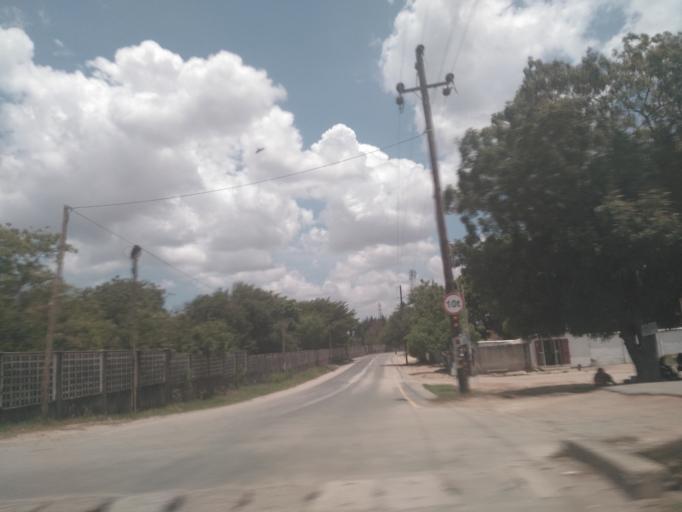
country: TZ
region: Dar es Salaam
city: Dar es Salaam
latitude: -6.8490
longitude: 39.2822
